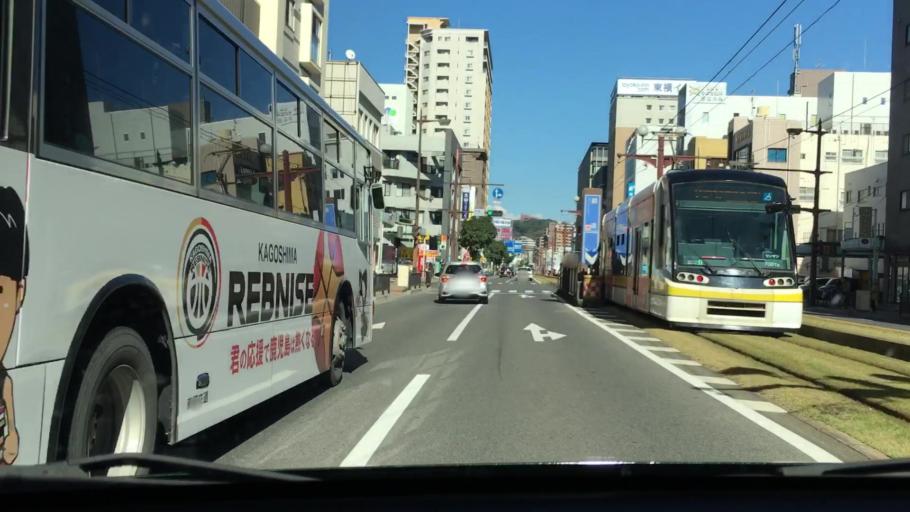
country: JP
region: Kagoshima
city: Kagoshima-shi
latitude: 31.5801
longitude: 130.5429
